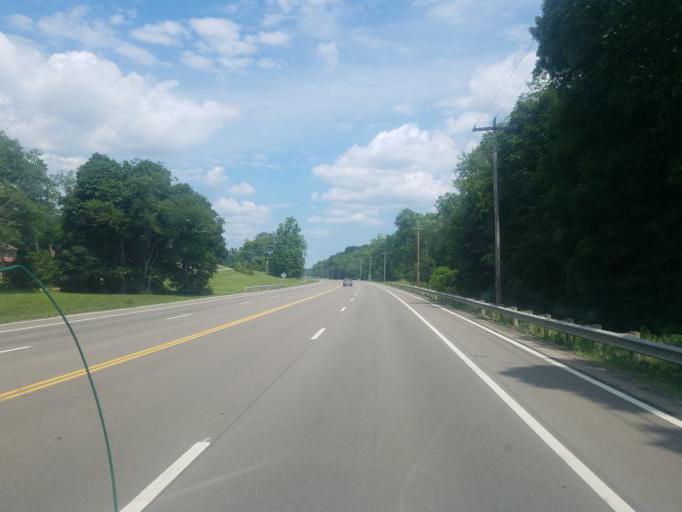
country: US
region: Ohio
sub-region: Muskingum County
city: Zanesville
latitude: 39.9500
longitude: -82.1106
